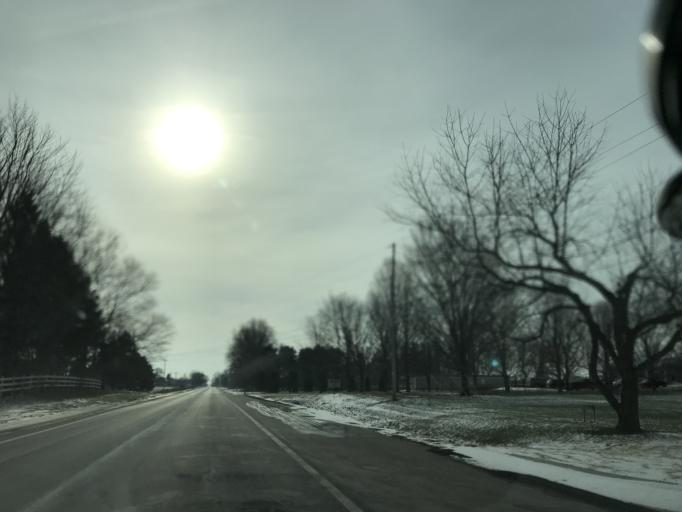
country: US
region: Michigan
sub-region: Ionia County
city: Lake Odessa
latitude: 42.8692
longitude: -85.0750
